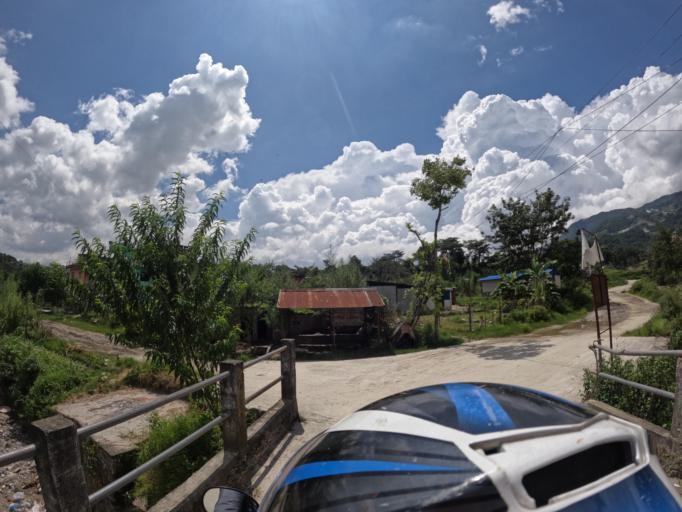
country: NP
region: Central Region
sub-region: Bagmati Zone
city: Kathmandu
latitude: 27.7865
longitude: 85.3259
